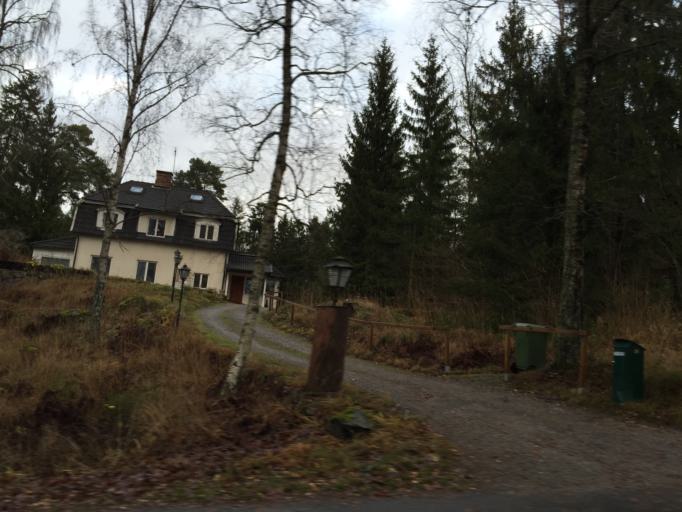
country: SE
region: Stockholm
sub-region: Salems Kommun
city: Ronninge
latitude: 59.1970
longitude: 17.7447
